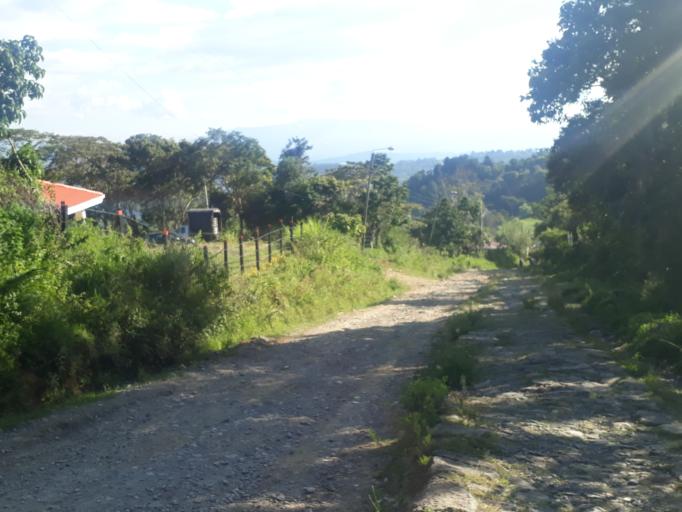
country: CO
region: Santander
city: Velez
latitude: 6.0265
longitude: -73.6670
